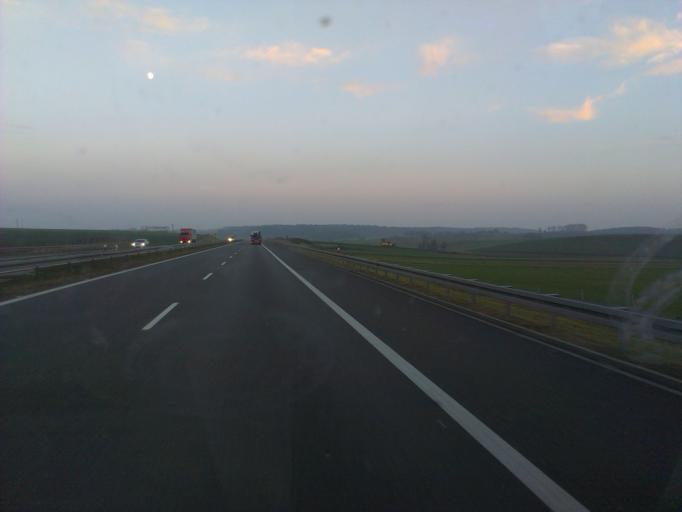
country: PL
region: Opole Voivodeship
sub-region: Powiat strzelecki
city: Lesnica
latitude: 50.4638
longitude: 18.2220
